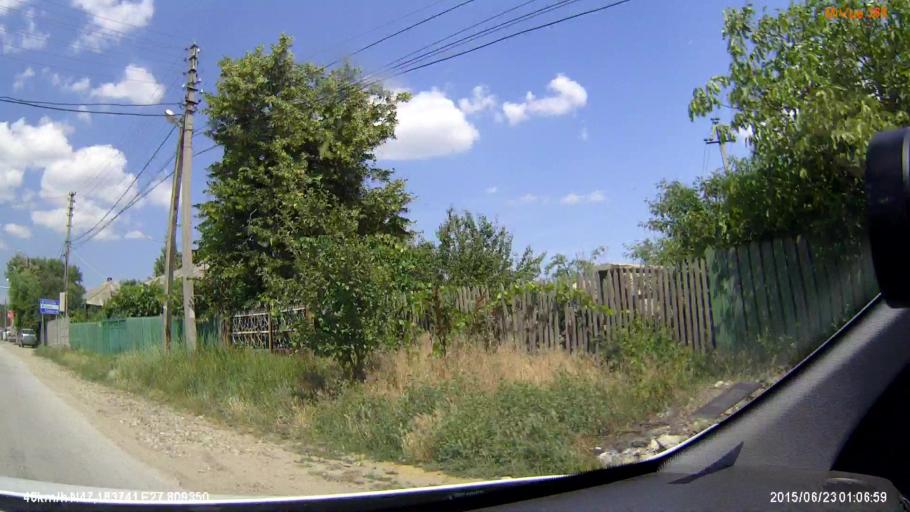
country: MD
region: Ungheni
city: Ungheni
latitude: 47.1836
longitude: 27.8093
